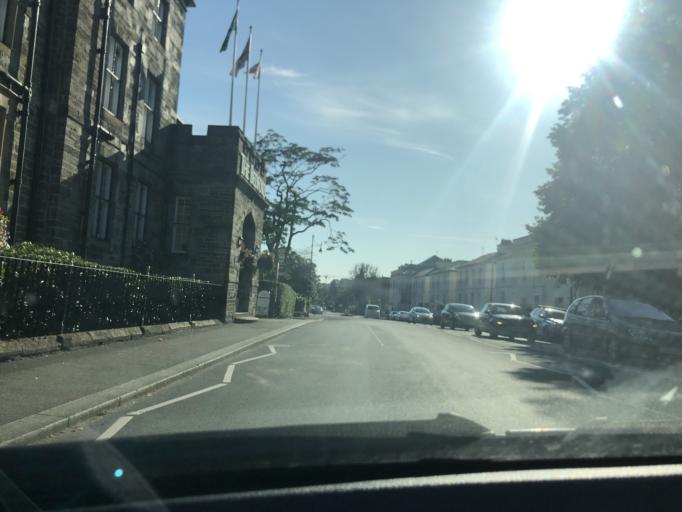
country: GB
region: England
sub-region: Devon
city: Tavistock
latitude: 50.5495
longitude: -4.1447
